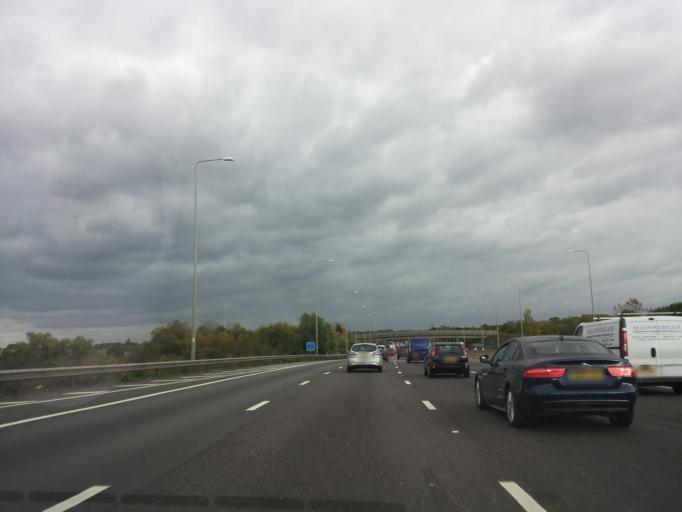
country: GB
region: England
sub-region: Hertfordshire
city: Radlett
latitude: 51.7119
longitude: -0.3155
